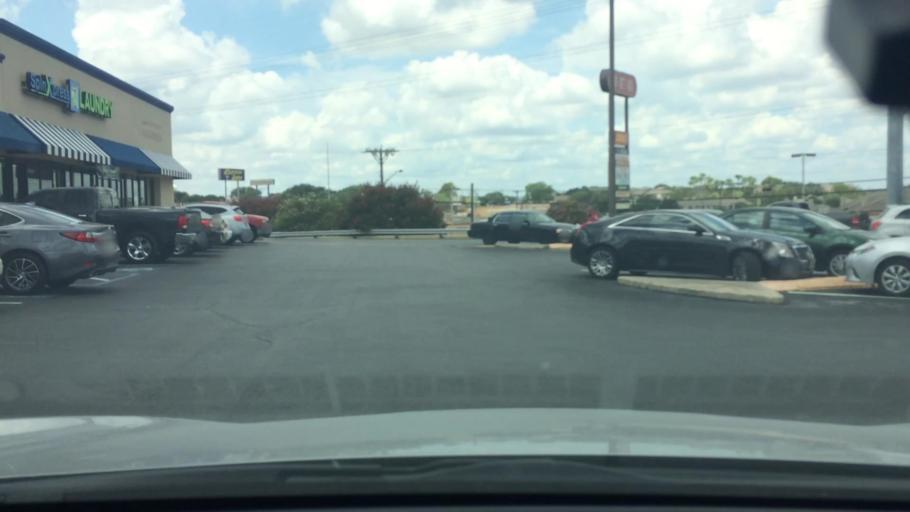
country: US
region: Texas
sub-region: Bexar County
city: Castle Hills
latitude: 29.5449
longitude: -98.5094
